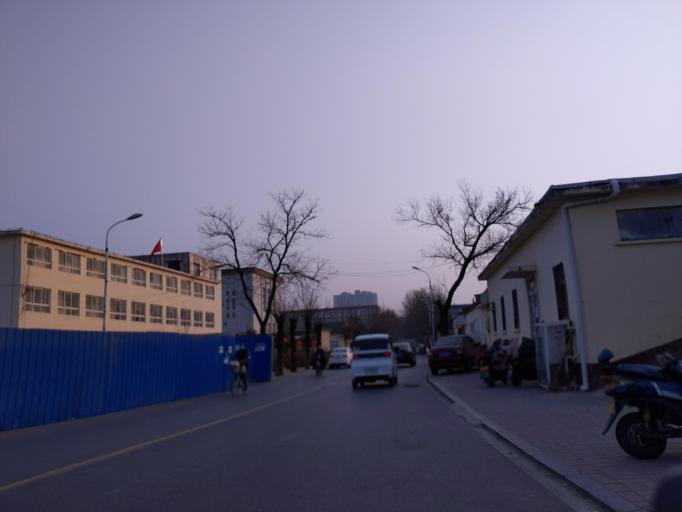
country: CN
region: Henan Sheng
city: Zhongyuanlu
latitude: 35.7857
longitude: 115.0637
